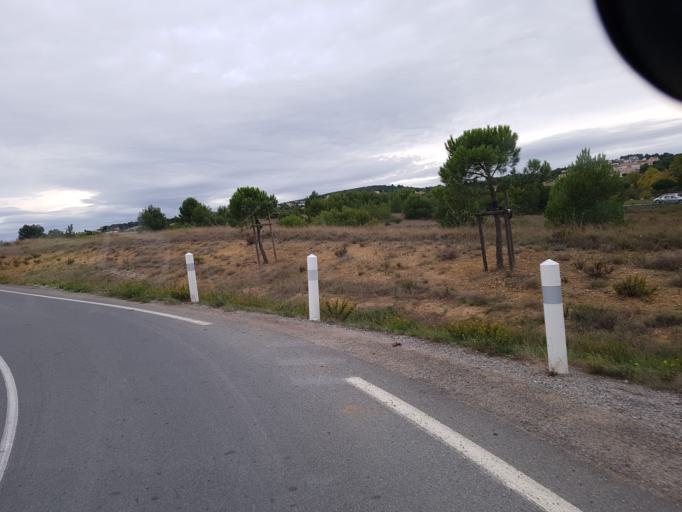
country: FR
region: Languedoc-Roussillon
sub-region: Departement de l'Aude
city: Narbonne
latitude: 43.1463
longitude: 2.9777
